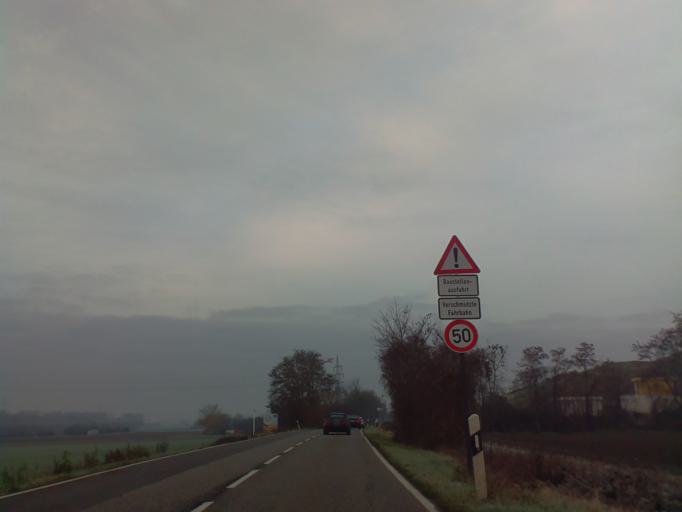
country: DE
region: Rheinland-Pfalz
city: Neuhofen
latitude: 49.4397
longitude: 8.4432
